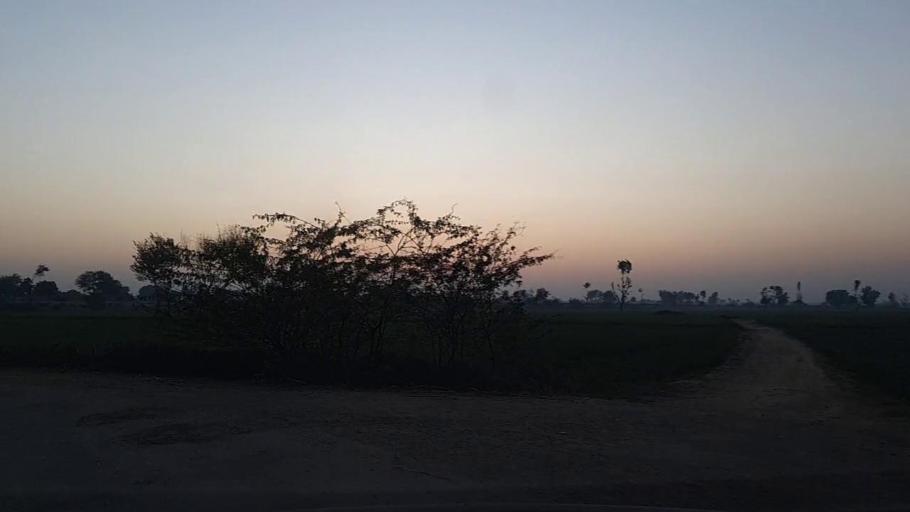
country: PK
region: Sindh
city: Daur
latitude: 26.4822
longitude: 68.4876
